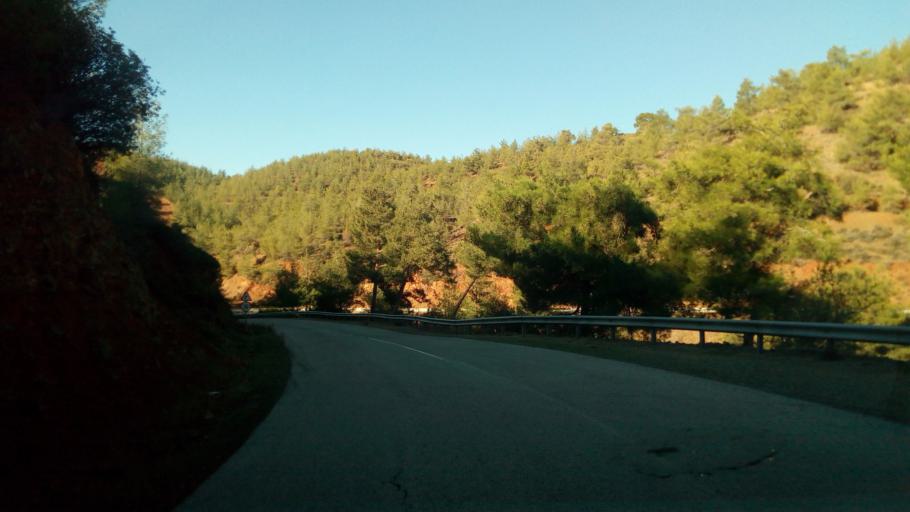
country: CY
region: Lefkosia
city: Lefka
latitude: 35.0671
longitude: 32.8163
